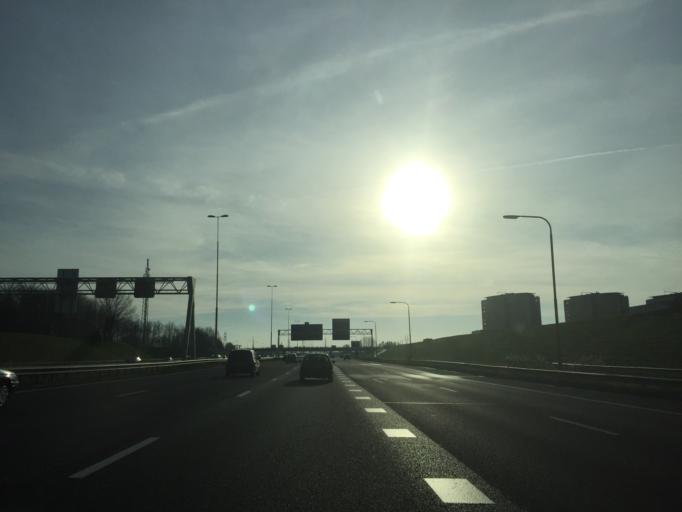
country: NL
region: South Holland
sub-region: Gemeente Capelle aan den IJssel
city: Capelle-West
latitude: 51.8894
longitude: 4.5619
